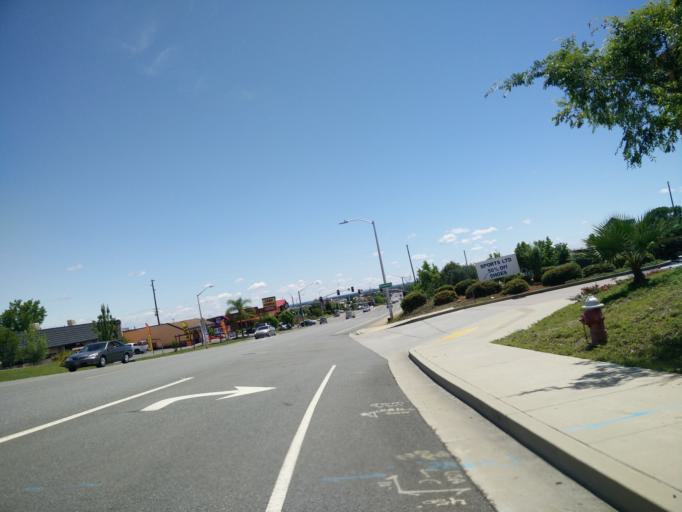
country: US
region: California
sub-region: Shasta County
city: Redding
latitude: 40.5944
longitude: -122.3586
